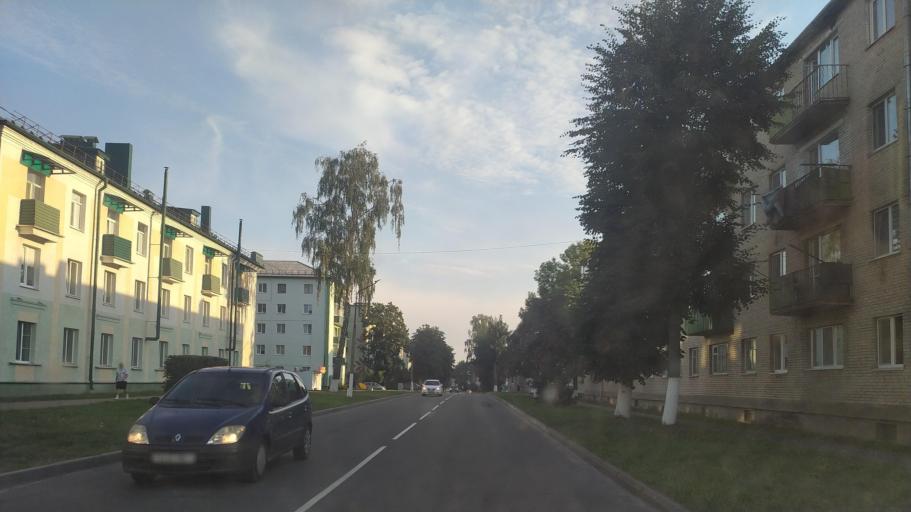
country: BY
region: Brest
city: Byaroza
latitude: 52.5404
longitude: 24.9842
